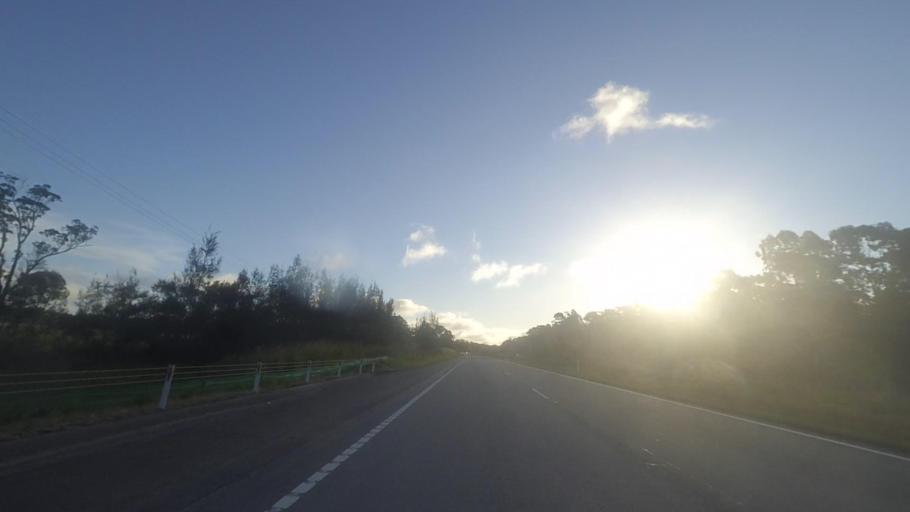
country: AU
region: New South Wales
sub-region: Great Lakes
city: Hawks Nest
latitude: -32.5416
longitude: 152.1664
